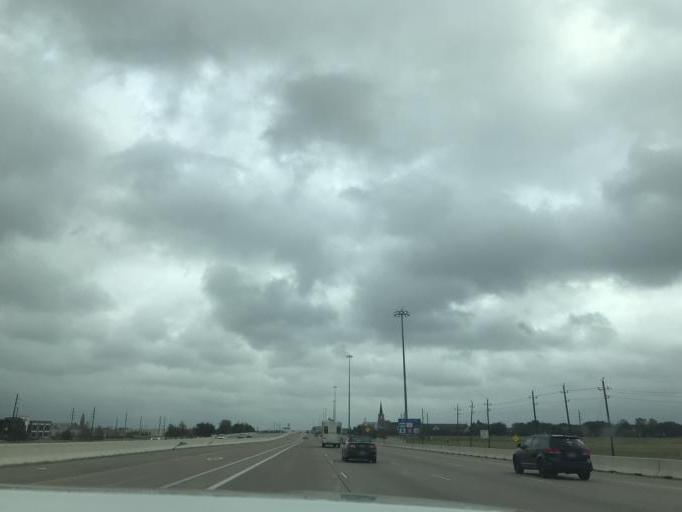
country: US
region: Texas
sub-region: Fort Bend County
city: Sugar Land
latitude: 29.5832
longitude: -95.6440
